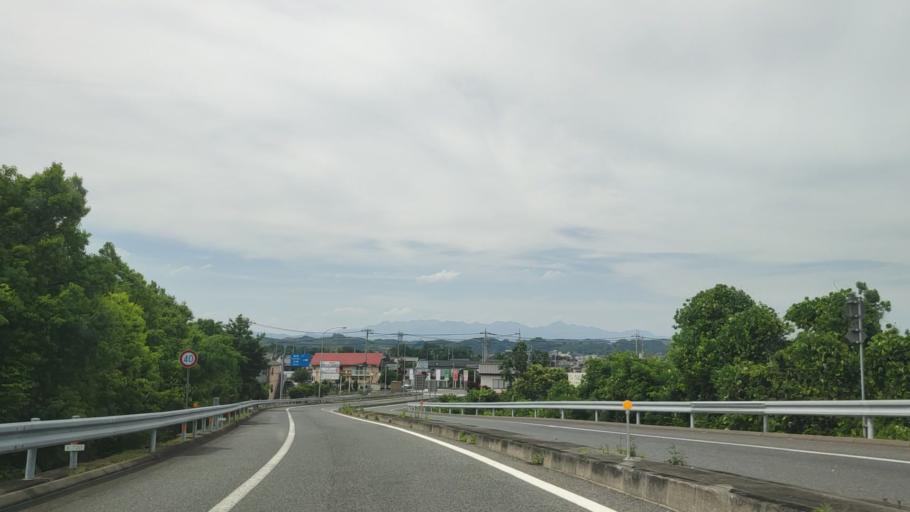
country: JP
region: Gunma
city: Tomioka
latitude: 36.2443
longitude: 138.8940
